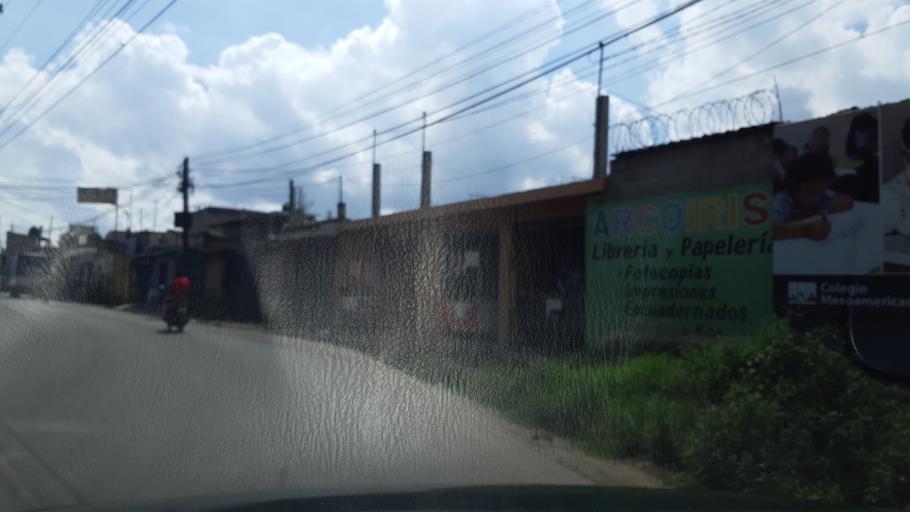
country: GT
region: Chimaltenango
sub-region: Municipio de Chimaltenango
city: Chimaltenango
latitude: 14.6620
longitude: -90.8111
